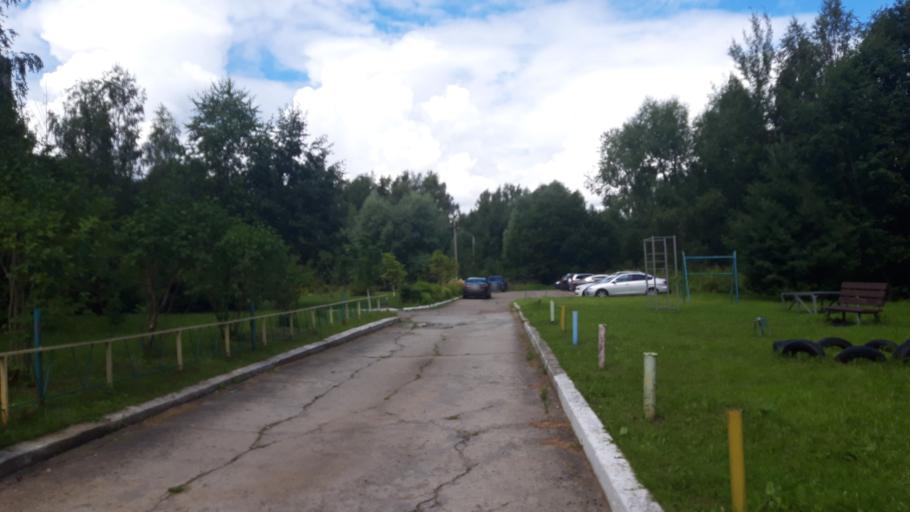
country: RU
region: Tverskaya
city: Konakovo
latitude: 56.6807
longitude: 36.6992
